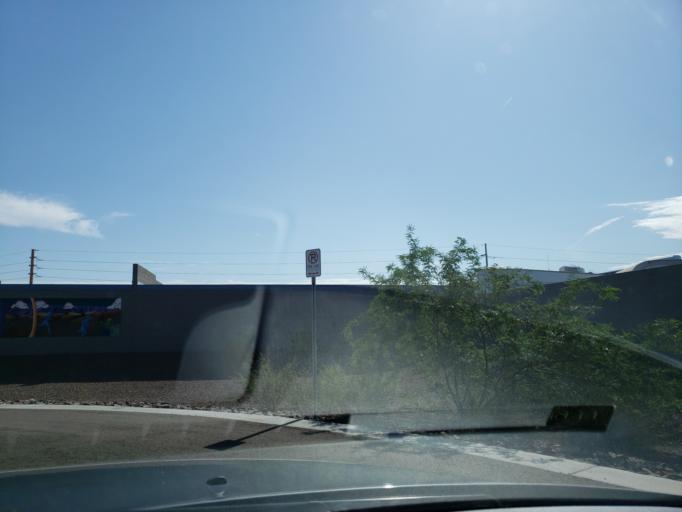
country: US
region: Arizona
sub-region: Maricopa County
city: Sun City
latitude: 33.6596
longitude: -112.2370
